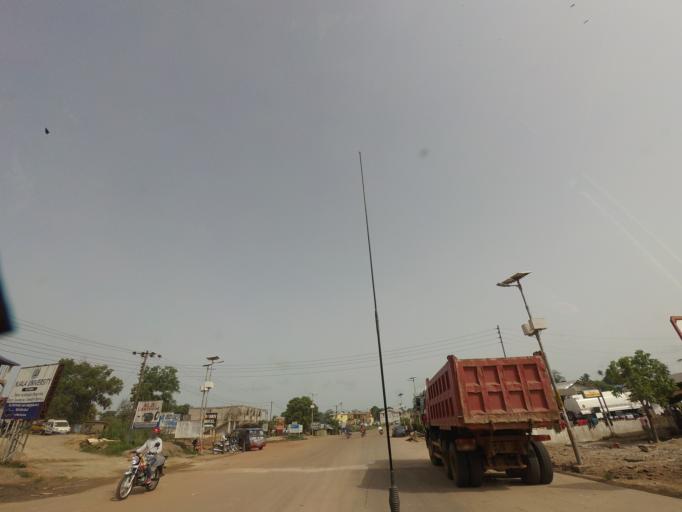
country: SL
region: Southern Province
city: Bo
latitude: 7.9523
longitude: -11.7518
